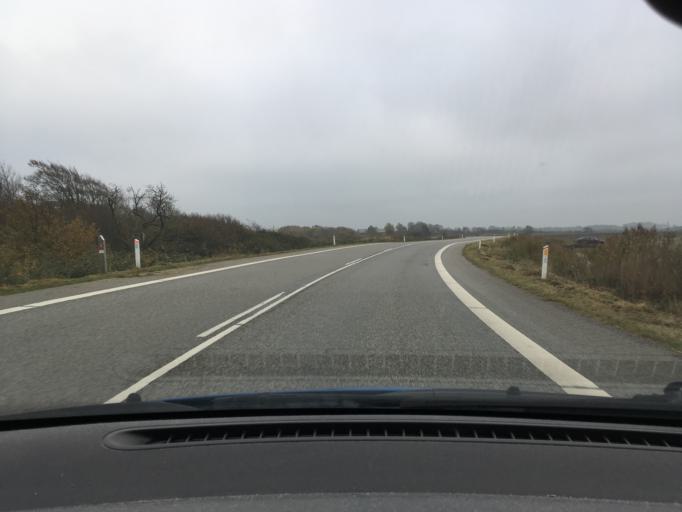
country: DE
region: Schleswig-Holstein
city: Aventoft
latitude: 54.9178
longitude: 8.8334
